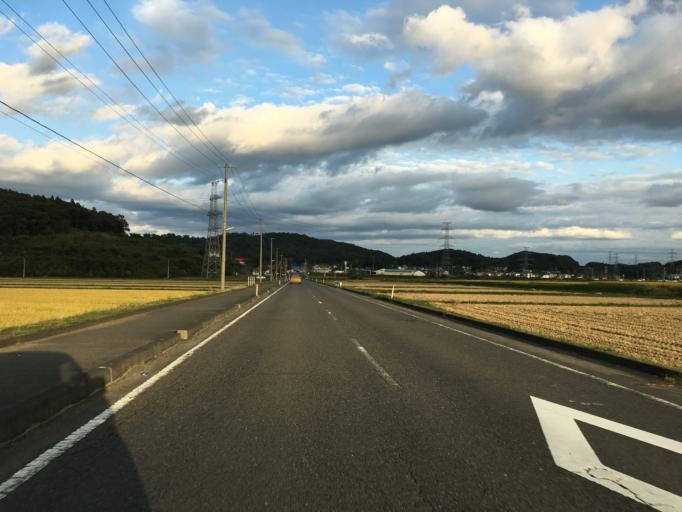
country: JP
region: Fukushima
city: Motomiya
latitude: 37.5454
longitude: 140.3916
